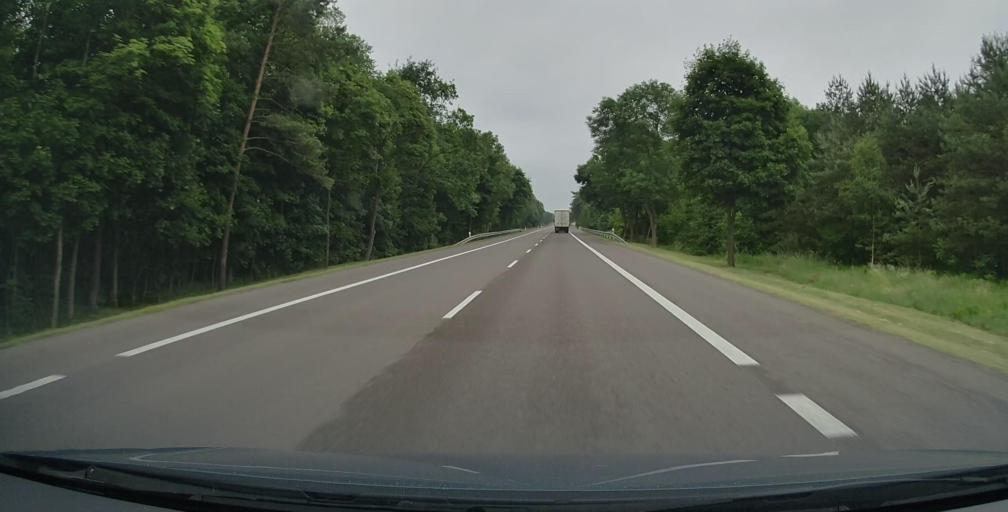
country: PL
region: Lublin Voivodeship
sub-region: Powiat bialski
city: Lesna Podlaska
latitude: 52.0372
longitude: 22.9807
